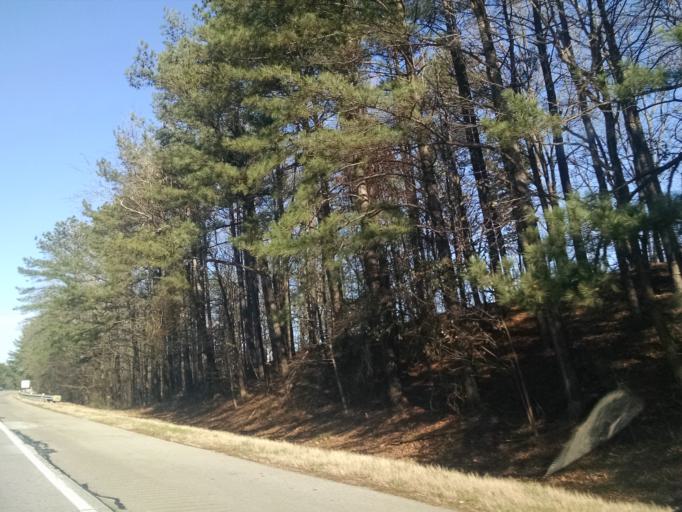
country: US
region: Georgia
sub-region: Gwinnett County
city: Suwanee
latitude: 34.0574
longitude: -84.0221
